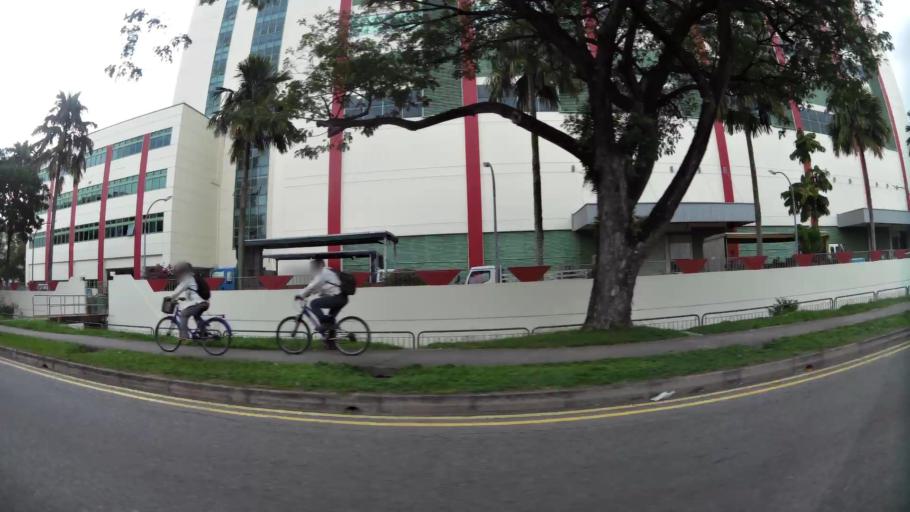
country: MY
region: Johor
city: Johor Bahru
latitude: 1.4631
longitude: 103.8104
